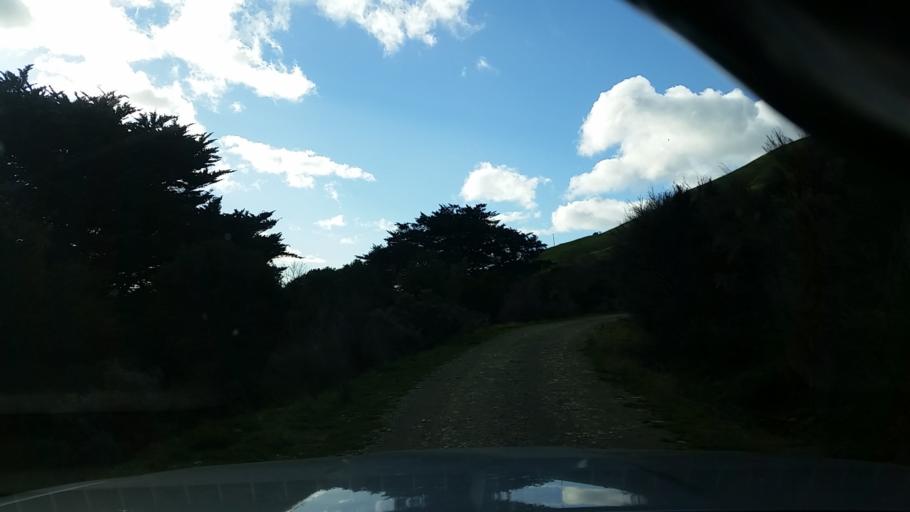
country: NZ
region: Marlborough
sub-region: Marlborough District
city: Picton
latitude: -41.0540
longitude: 174.1097
